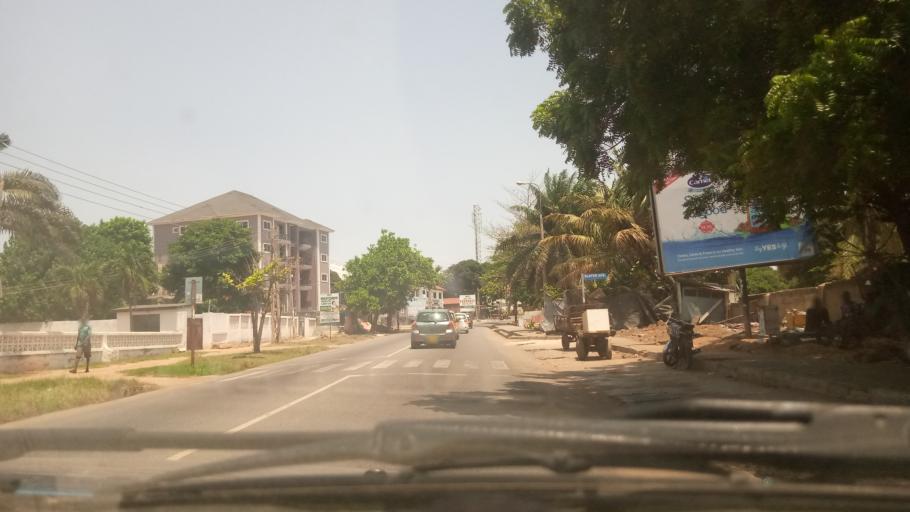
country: GH
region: Greater Accra
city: Accra
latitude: 5.5437
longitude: -0.2399
